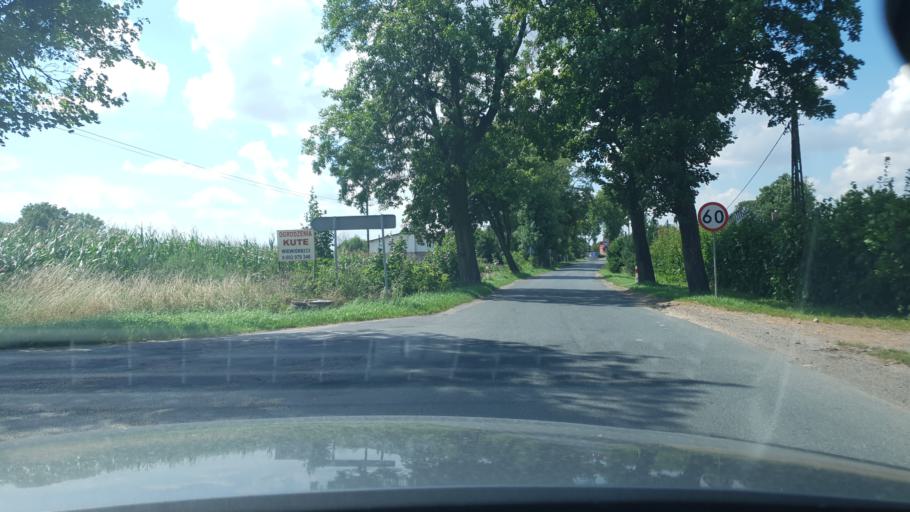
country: PL
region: Kujawsko-Pomorskie
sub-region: Powiat wabrzeski
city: Pluznica
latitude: 53.3671
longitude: 18.8058
